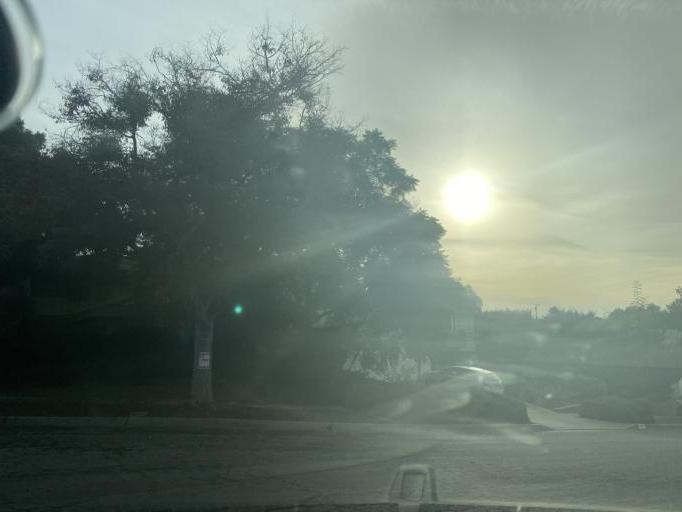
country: US
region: California
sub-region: Orange County
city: Brea
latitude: 33.9000
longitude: -117.8790
